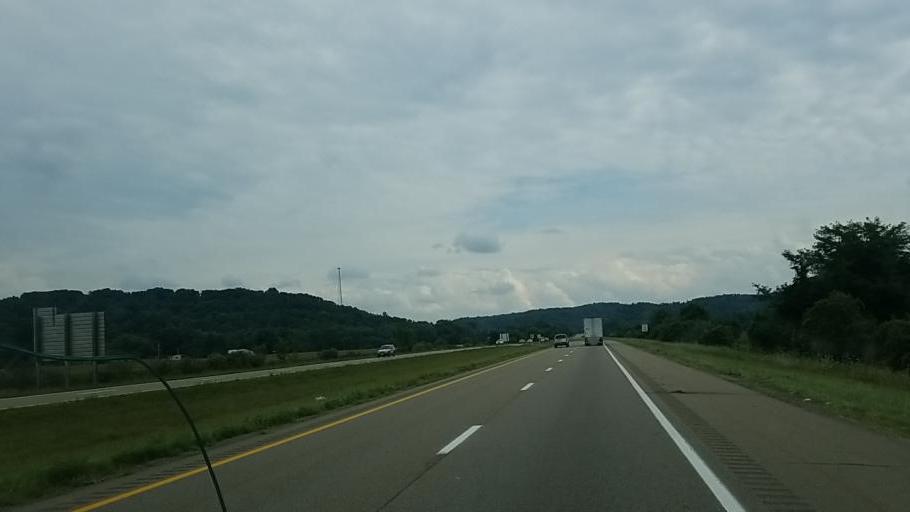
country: US
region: Ohio
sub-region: Tuscarawas County
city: Newcomerstown
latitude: 40.2822
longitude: -81.5516
